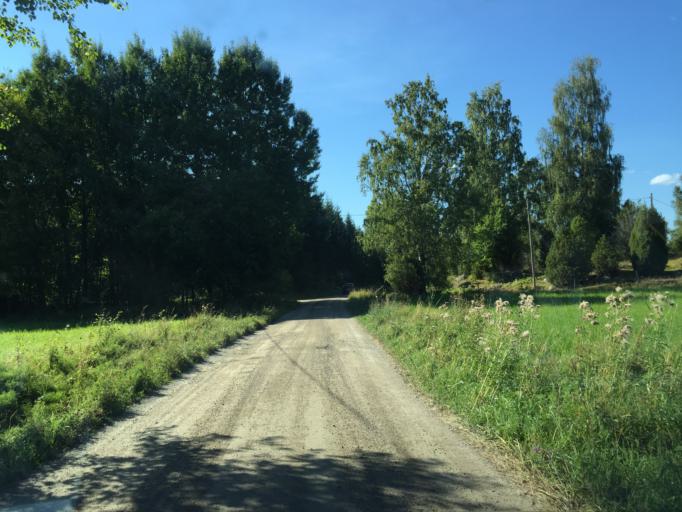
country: SE
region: OEstergoetland
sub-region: Finspangs Kommun
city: Finspang
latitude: 58.8905
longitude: 15.7187
